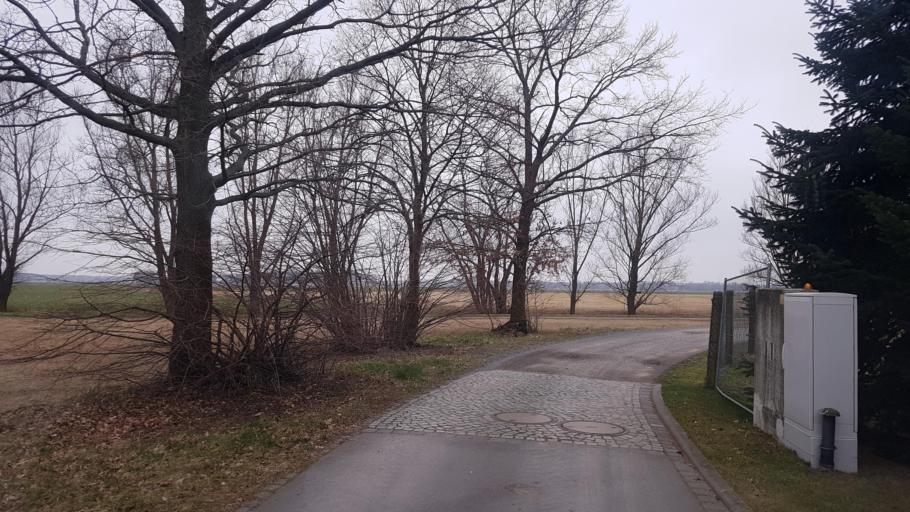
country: DE
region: Brandenburg
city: Herzberg
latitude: 51.6831
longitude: 13.2737
